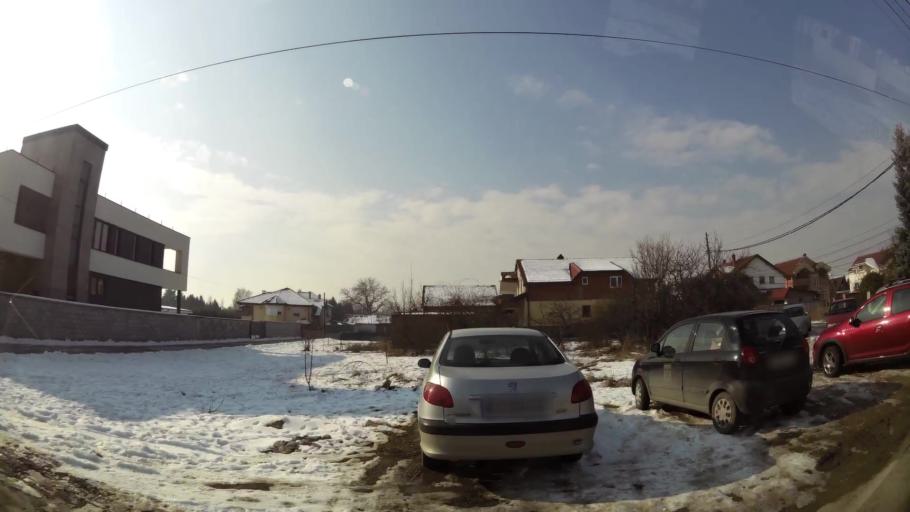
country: MK
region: Suto Orizari
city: Suto Orizare
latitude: 42.0265
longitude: 21.3878
